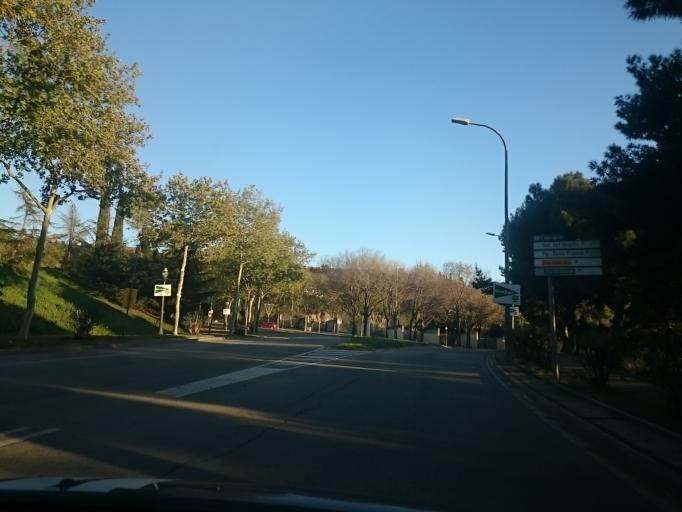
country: ES
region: Catalonia
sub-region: Provincia de Barcelona
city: Sants-Montjuic
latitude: 41.3606
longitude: 2.1493
